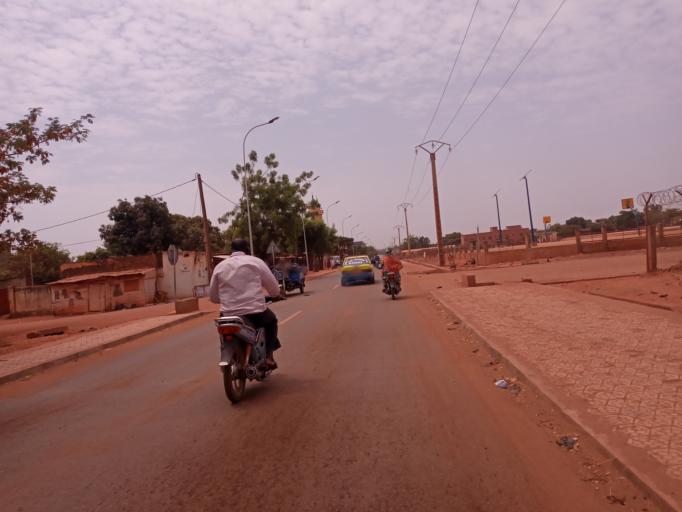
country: ML
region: Bamako
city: Bamako
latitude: 12.5850
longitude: -7.9882
